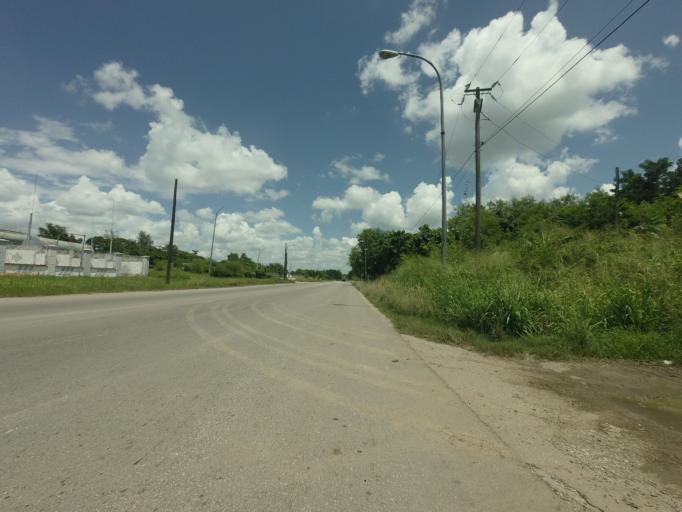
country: CU
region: La Habana
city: Arroyo Naranjo
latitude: 23.0359
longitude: -82.3484
